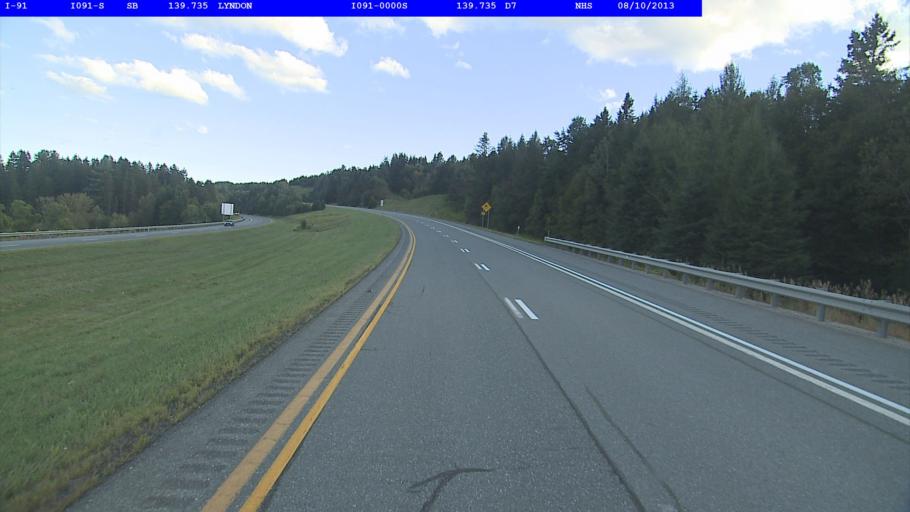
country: US
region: Vermont
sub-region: Caledonia County
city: Lyndonville
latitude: 44.5510
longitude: -72.0291
